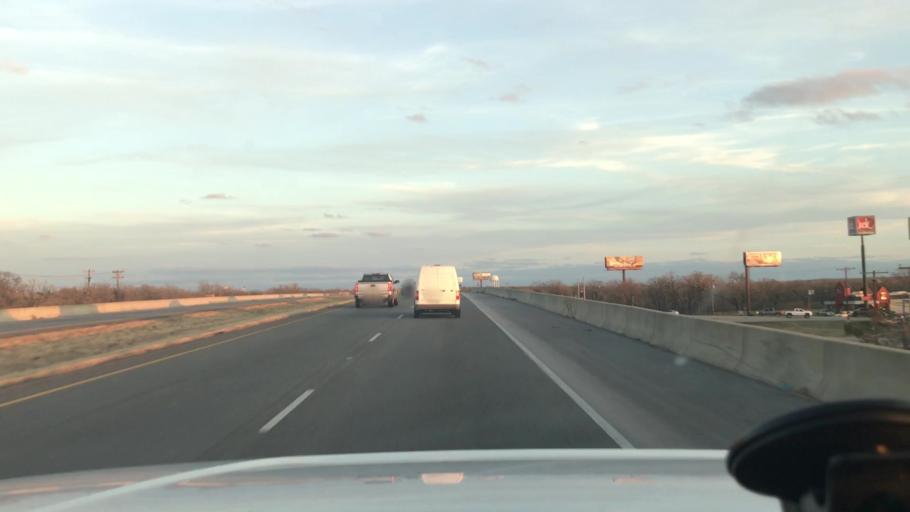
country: US
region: Texas
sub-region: Bastrop County
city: Wyldwood
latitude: 30.1134
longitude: -97.4172
